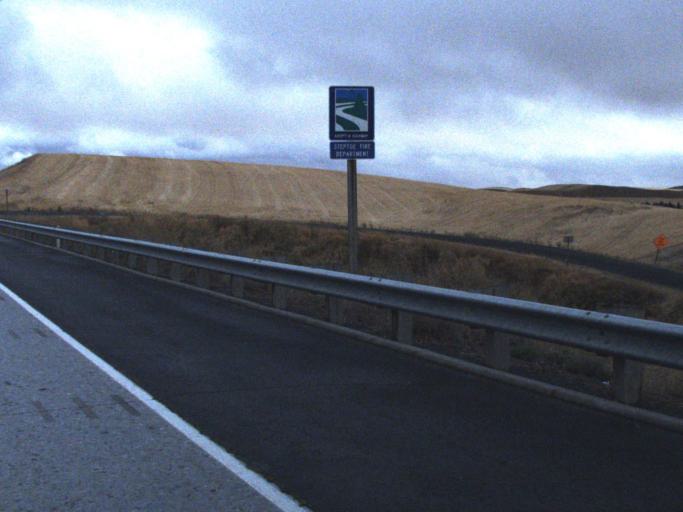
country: US
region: Washington
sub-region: Whitman County
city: Colfax
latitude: 47.0207
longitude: -117.3579
